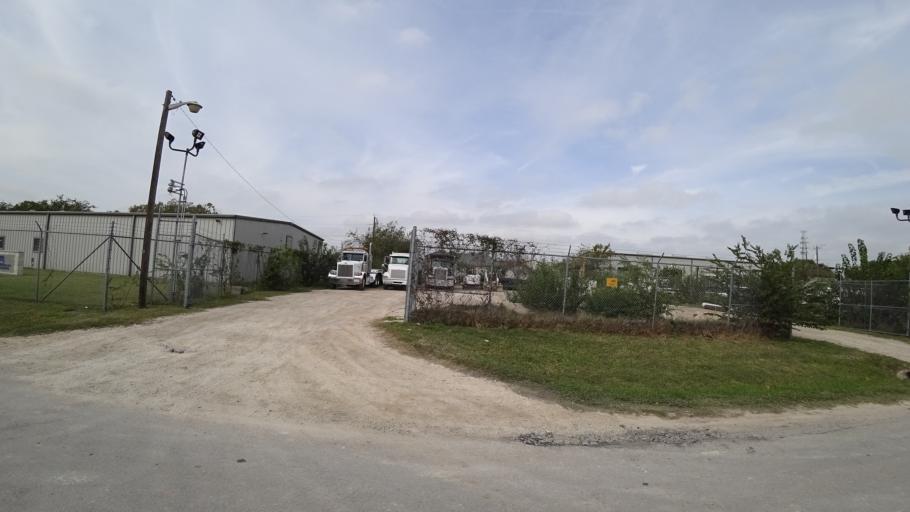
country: US
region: Texas
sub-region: Travis County
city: Wells Branch
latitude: 30.4503
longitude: -97.6683
